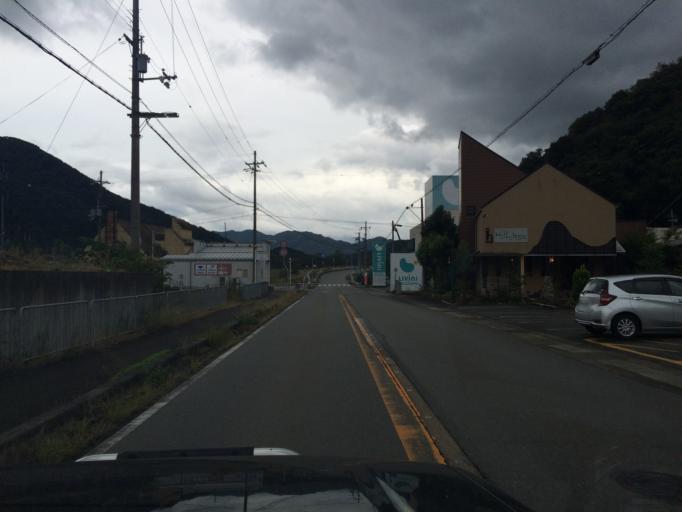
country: JP
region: Hyogo
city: Toyooka
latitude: 35.4546
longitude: 134.7730
